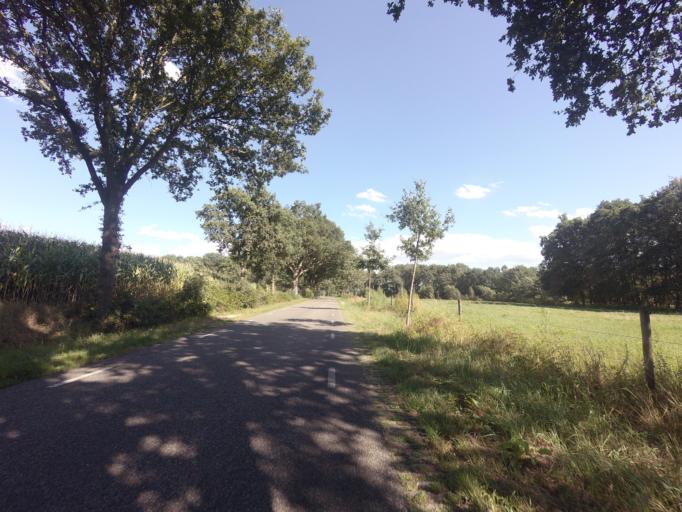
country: NL
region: Drenthe
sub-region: Gemeente Hoogeveen
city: Hoogeveen
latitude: 52.6469
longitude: 6.5112
